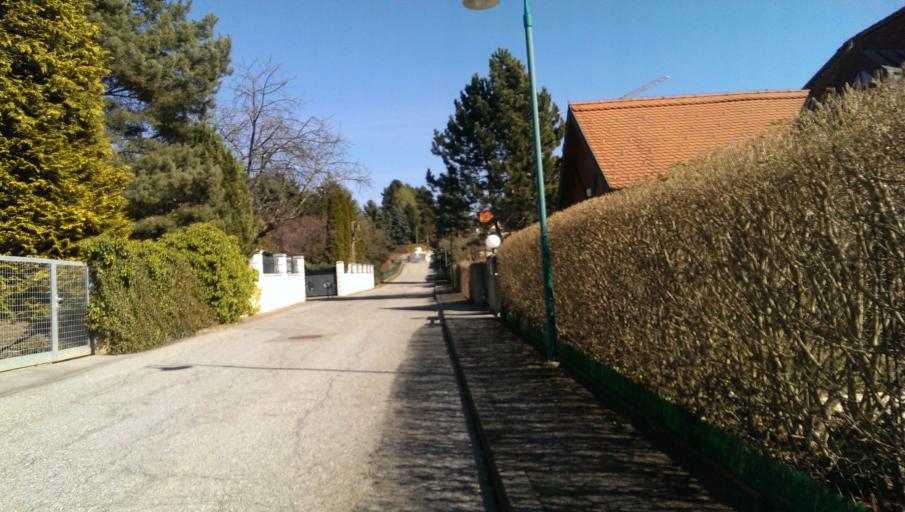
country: AT
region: Styria
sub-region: Graz Stadt
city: Graz
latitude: 47.0647
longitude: 15.4774
